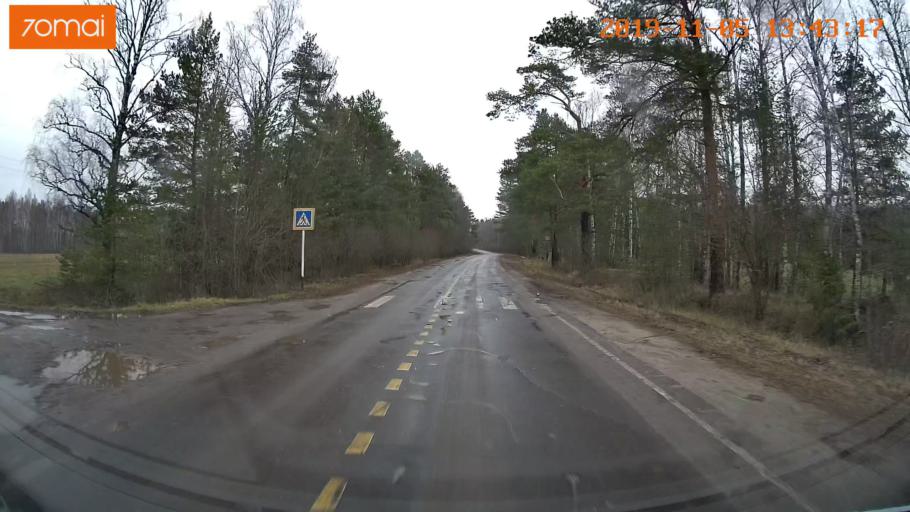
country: RU
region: Ivanovo
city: Shuya
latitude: 56.9725
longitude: 41.4016
